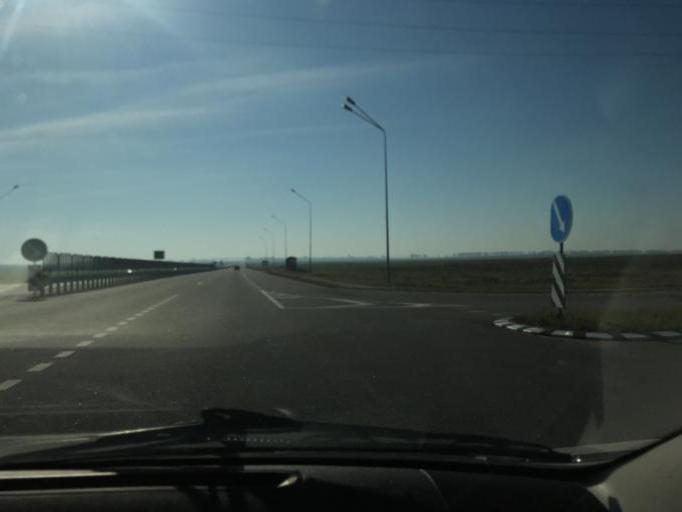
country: BY
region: Minsk
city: Slutsk
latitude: 53.1763
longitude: 27.5512
